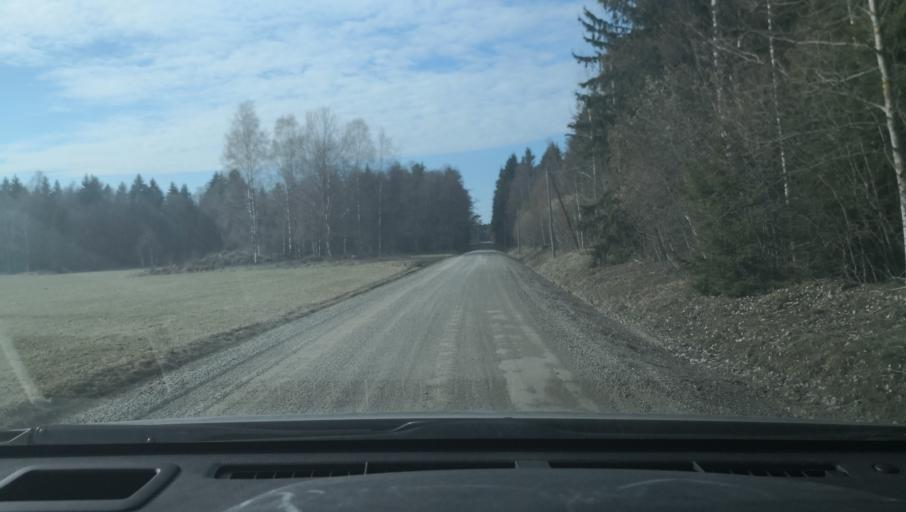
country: SE
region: Uppsala
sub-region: Heby Kommun
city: Heby
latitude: 59.8444
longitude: 16.8979
